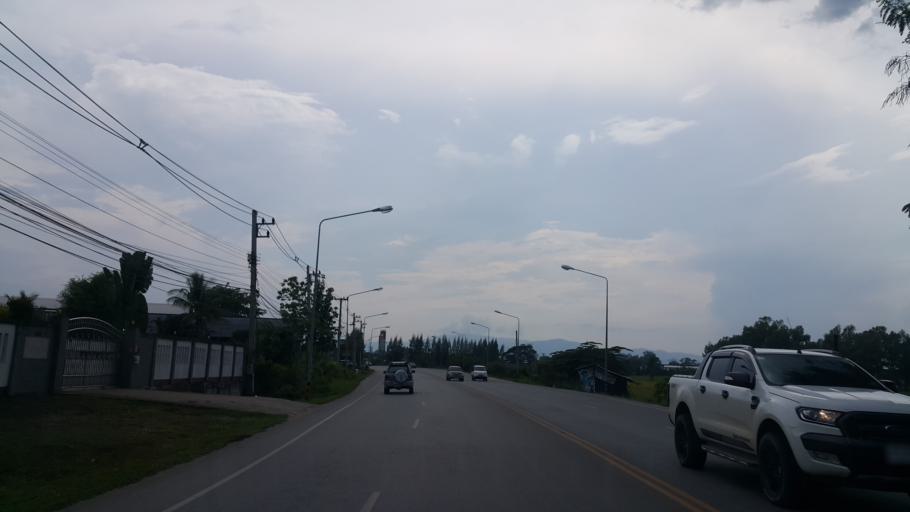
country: TH
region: Chiang Rai
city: Chiang Rai
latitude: 19.9131
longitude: 99.8682
